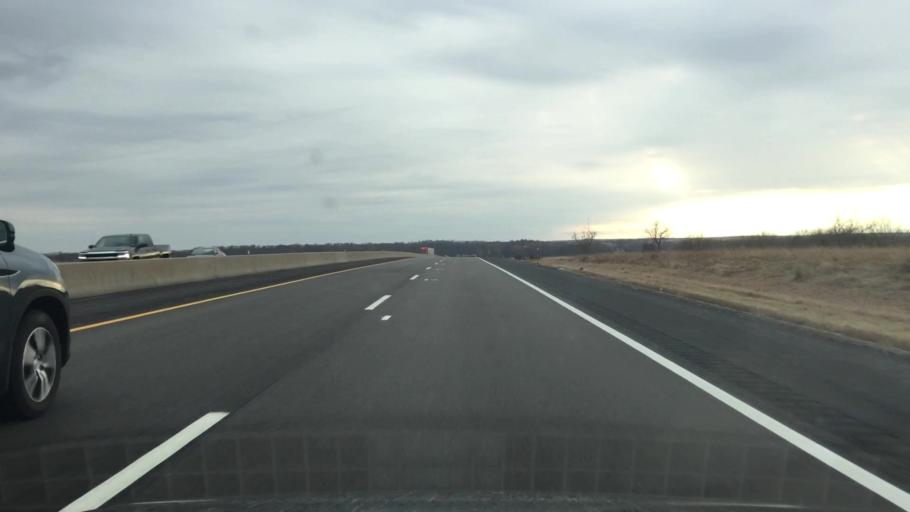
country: US
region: Kansas
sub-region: Osage County
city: Osage City
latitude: 38.6771
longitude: -96.0060
